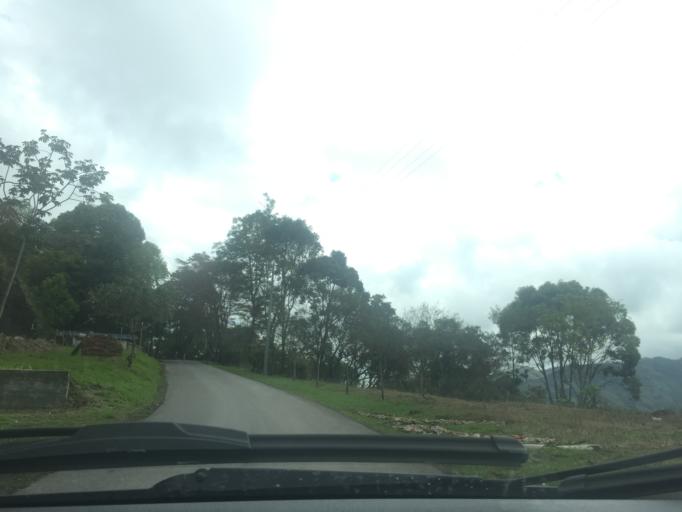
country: CO
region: Cundinamarca
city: Supata
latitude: 5.0535
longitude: -74.2372
